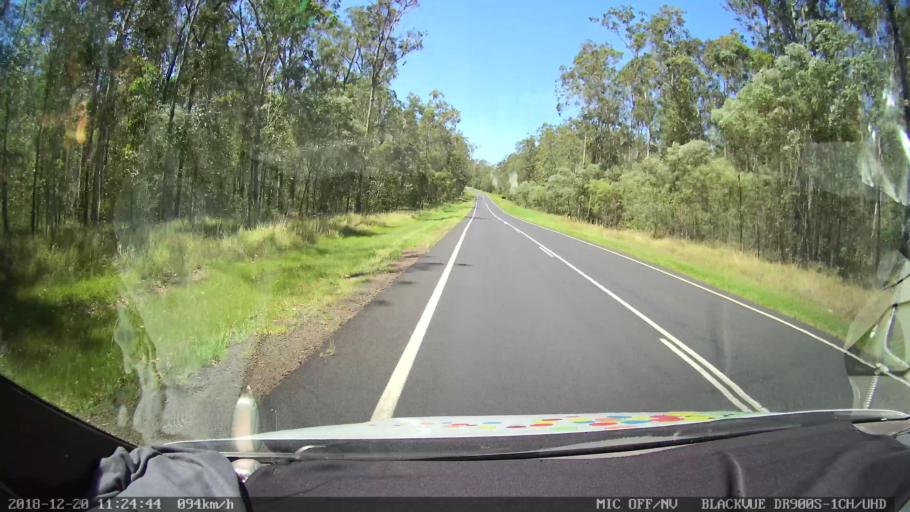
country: AU
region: New South Wales
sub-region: Richmond Valley
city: Casino
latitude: -29.0782
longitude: 153.0010
